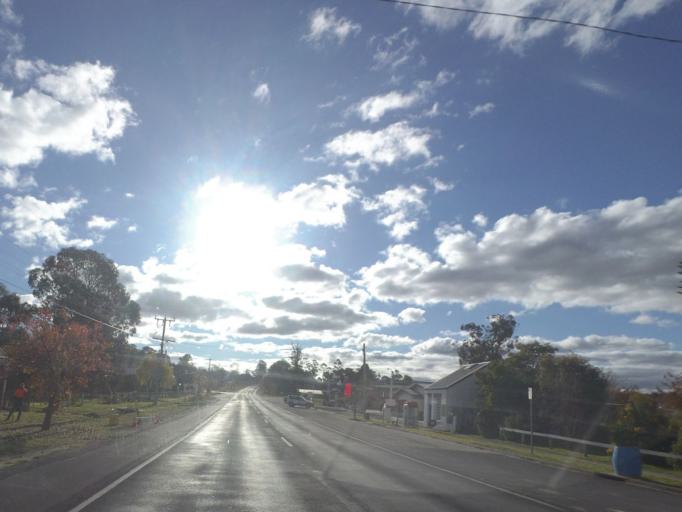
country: AU
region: Victoria
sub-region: Mount Alexander
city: Castlemaine
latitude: -37.1391
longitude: 144.3488
